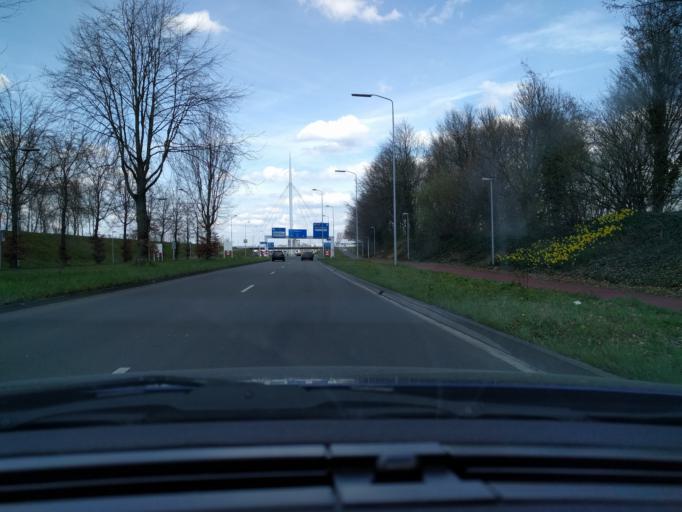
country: NL
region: North Brabant
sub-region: Gemeente Eindhoven
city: Meerhoven
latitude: 51.4310
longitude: 5.4163
